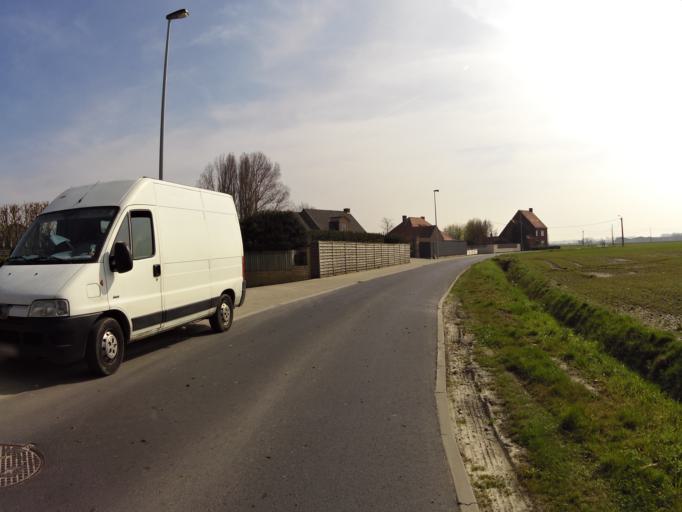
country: BE
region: Flanders
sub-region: Provincie West-Vlaanderen
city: Oudenburg
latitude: 51.1803
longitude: 2.9805
